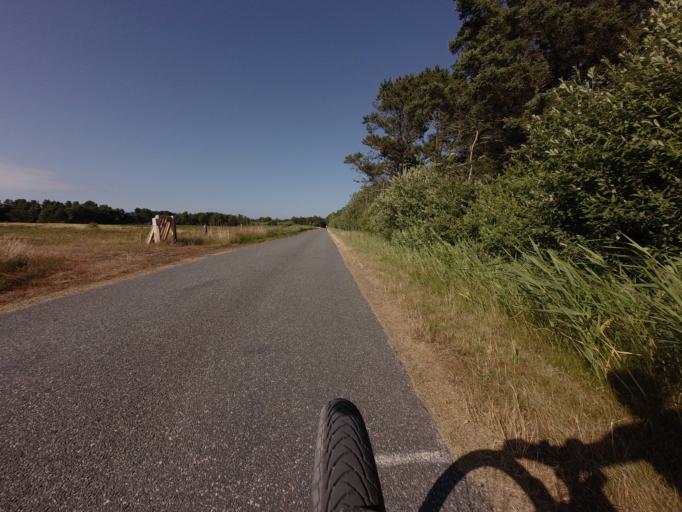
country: DK
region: North Denmark
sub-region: Laeso Kommune
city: Byrum
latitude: 57.2600
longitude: 10.8881
